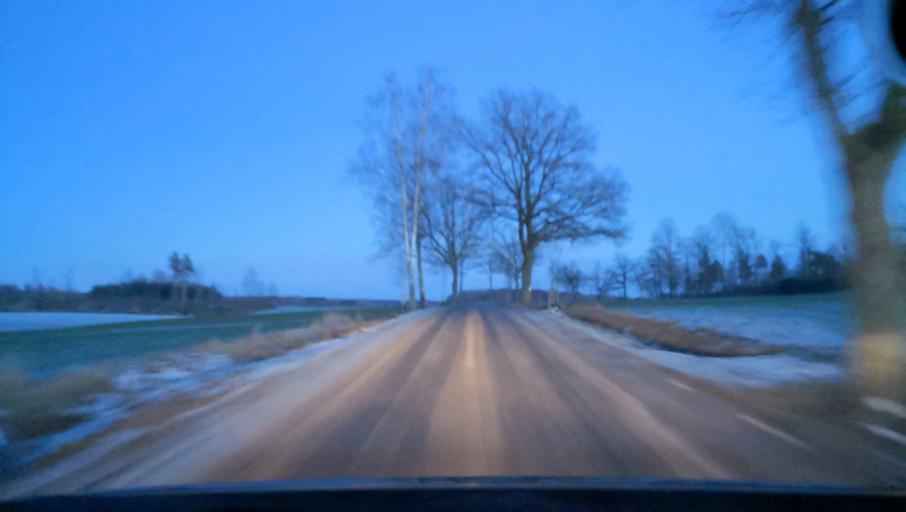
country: SE
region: Soedermanland
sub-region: Katrineholms Kommun
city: Katrineholm
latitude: 59.0770
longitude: 16.3287
